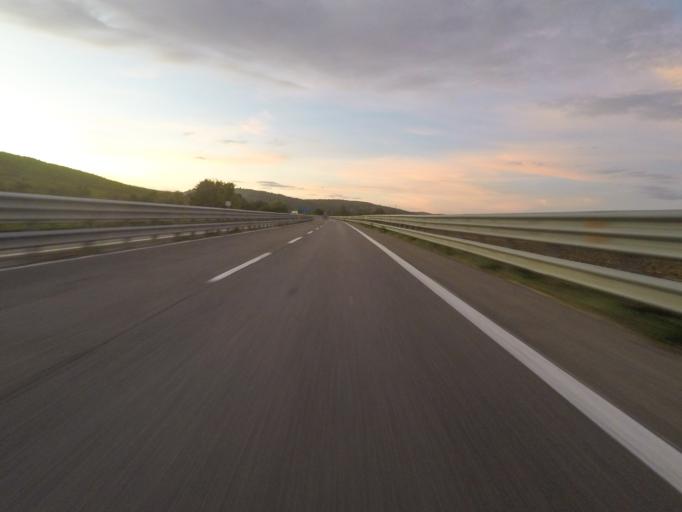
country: IT
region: Tuscany
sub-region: Province of Arezzo
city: Lucignano
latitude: 43.2493
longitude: 11.7172
